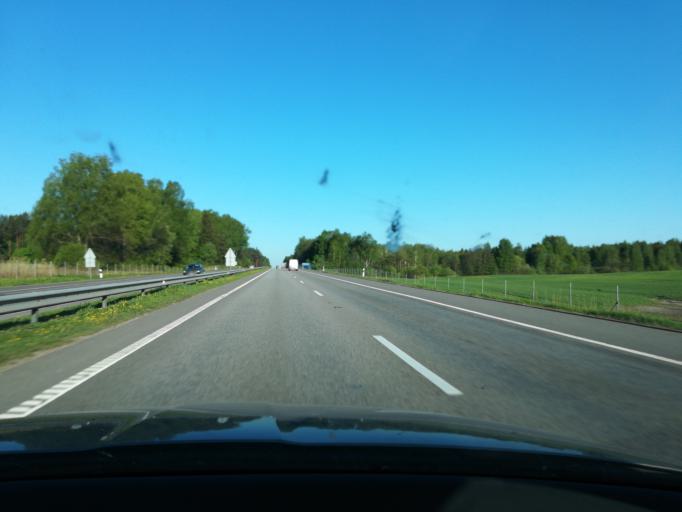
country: LT
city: Ziezmariai
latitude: 54.7984
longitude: 24.5430
